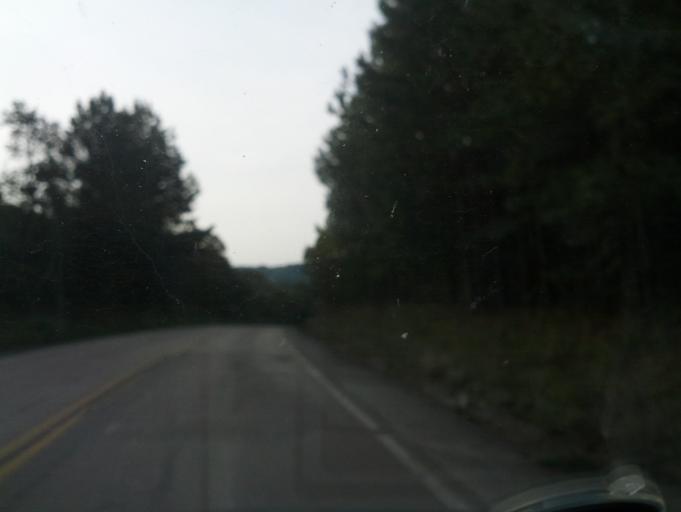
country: BR
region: Santa Catarina
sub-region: Otacilio Costa
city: Otacilio Costa
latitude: -27.3164
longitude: -50.1370
